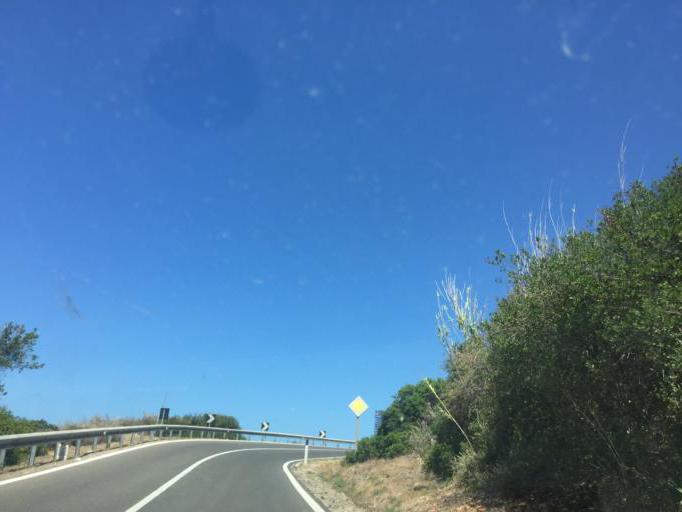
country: IT
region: Sardinia
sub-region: Provincia di Sassari
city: Castelsardo
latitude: 40.9111
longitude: 8.7239
